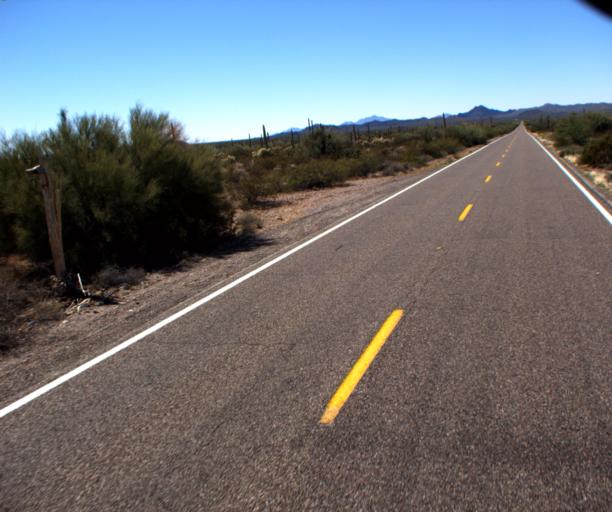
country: MX
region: Sonora
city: Sonoyta
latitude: 32.0587
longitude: -112.7880
